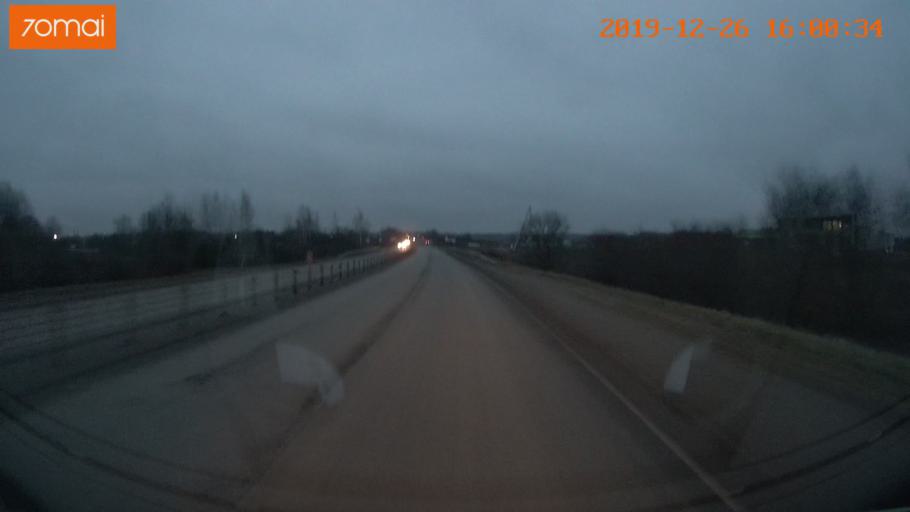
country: RU
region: Jaroslavl
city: Rybinsk
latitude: 58.0230
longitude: 38.8041
